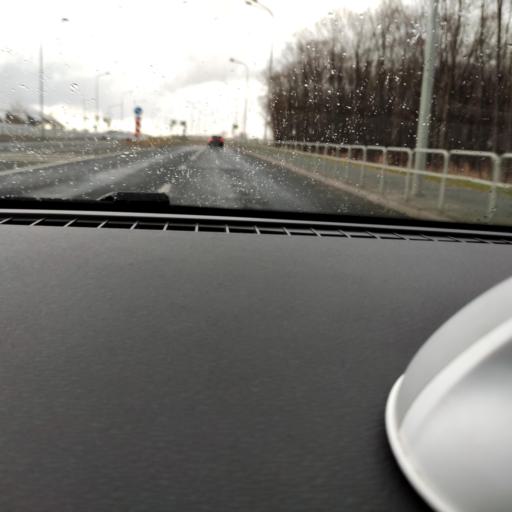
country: RU
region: Samara
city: Petra-Dubrava
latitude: 53.2794
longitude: 50.2504
